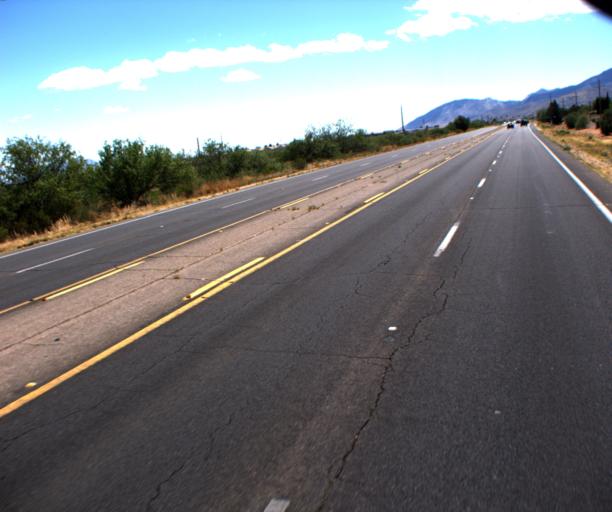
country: US
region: Arizona
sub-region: Cochise County
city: Sierra Vista
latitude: 31.5156
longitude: -110.2574
